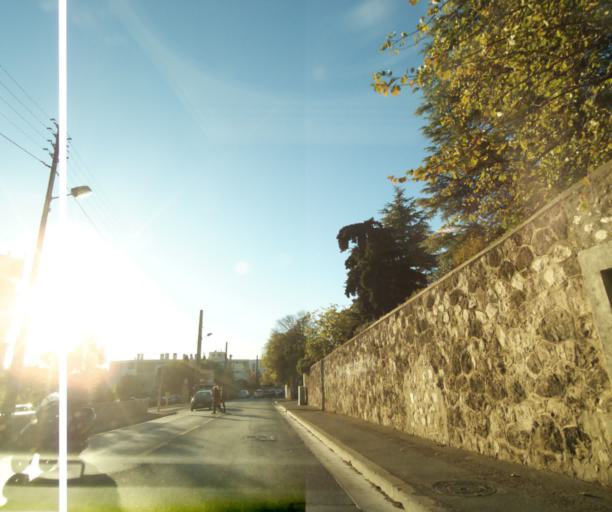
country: FR
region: Provence-Alpes-Cote d'Azur
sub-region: Departement des Bouches-du-Rhone
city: Marseille 12
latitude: 43.3079
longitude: 5.4298
